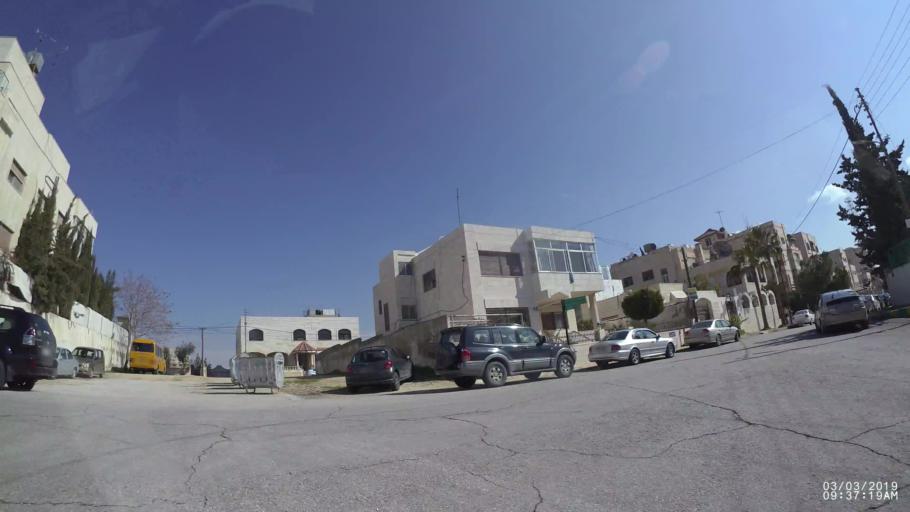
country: JO
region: Amman
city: Al Jubayhah
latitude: 31.9997
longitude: 35.8929
